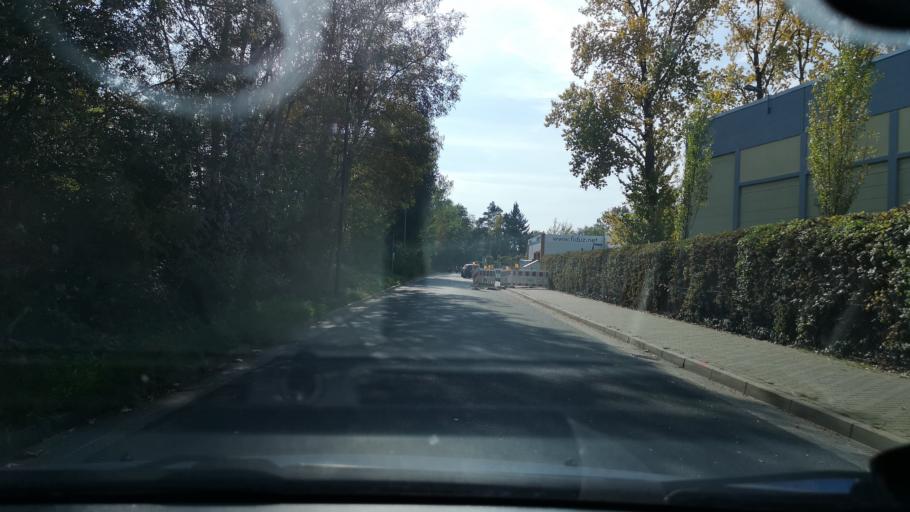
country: DE
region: Lower Saxony
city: Langenhagen
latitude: 52.4565
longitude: 9.7391
